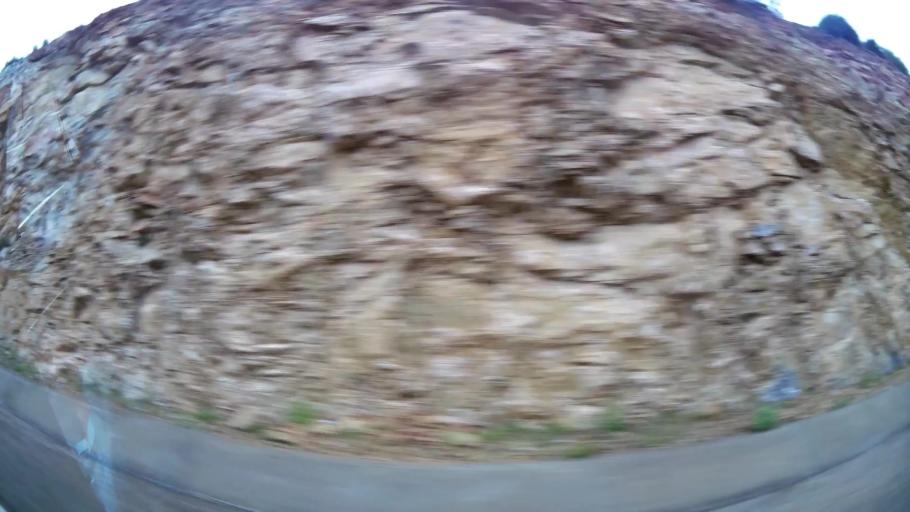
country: MA
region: Taza-Al Hoceima-Taounate
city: Al Hoceima
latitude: 35.2300
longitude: -3.9303
